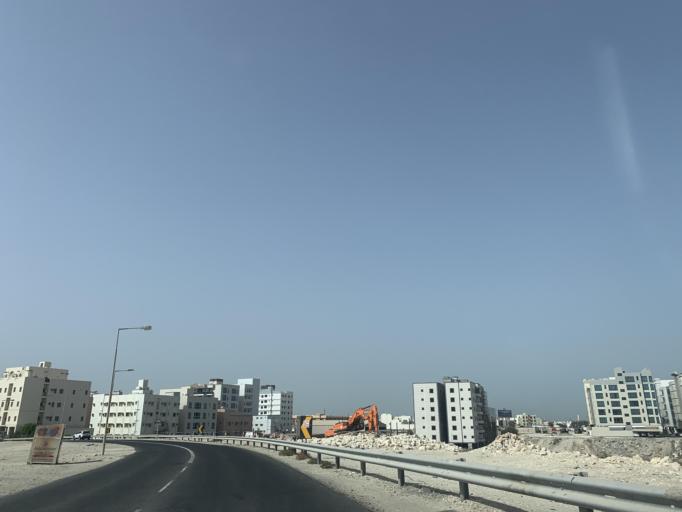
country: BH
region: Northern
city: Ar Rifa'
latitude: 26.1479
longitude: 50.5697
